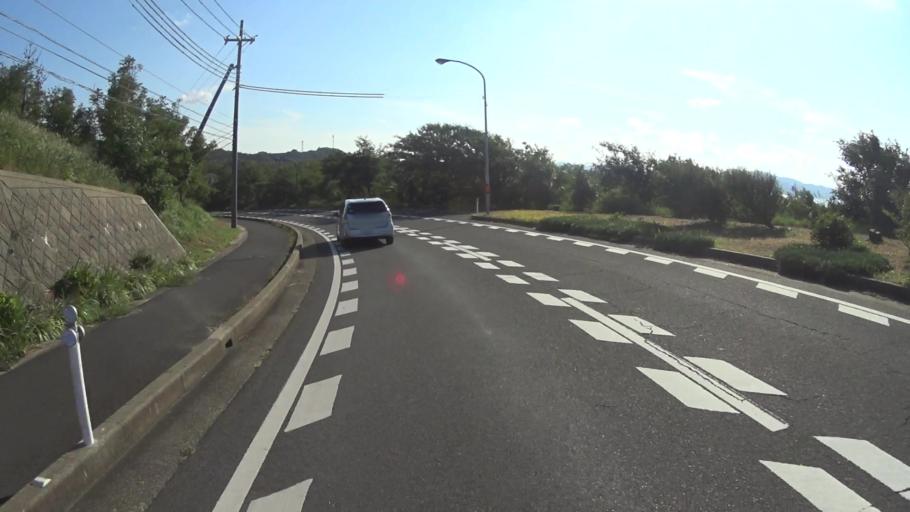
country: JP
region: Hyogo
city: Toyooka
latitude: 35.6614
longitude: 134.9643
